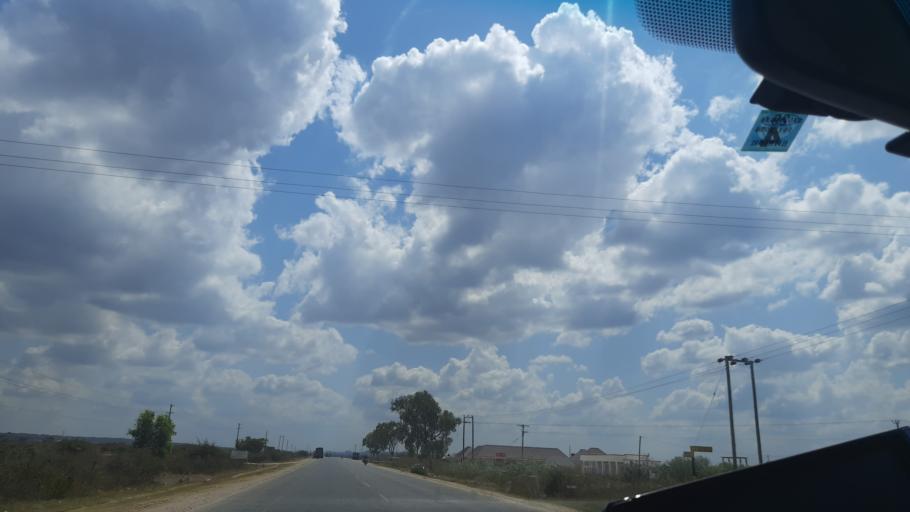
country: TZ
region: Dodoma
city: Dodoma
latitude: -6.1420
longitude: 35.6956
